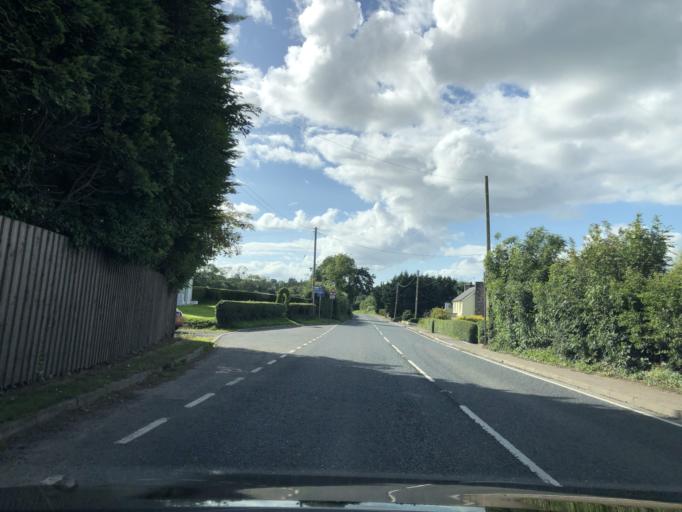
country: GB
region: Northern Ireland
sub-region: Castlereagh District
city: Dundonald
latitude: 54.5743
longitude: -5.7812
